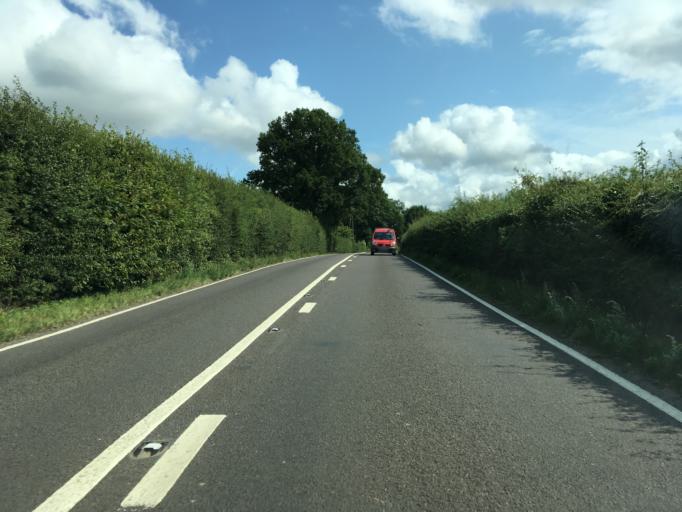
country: GB
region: England
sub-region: Kent
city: Headcorn
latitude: 51.1962
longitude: 0.5985
